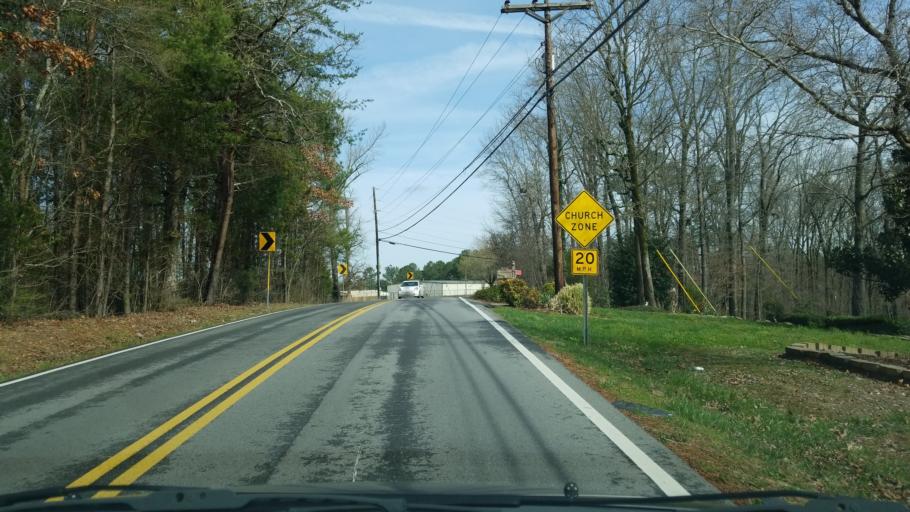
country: US
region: Tennessee
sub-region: Hamilton County
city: Lakesite
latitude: 35.1645
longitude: -85.0596
